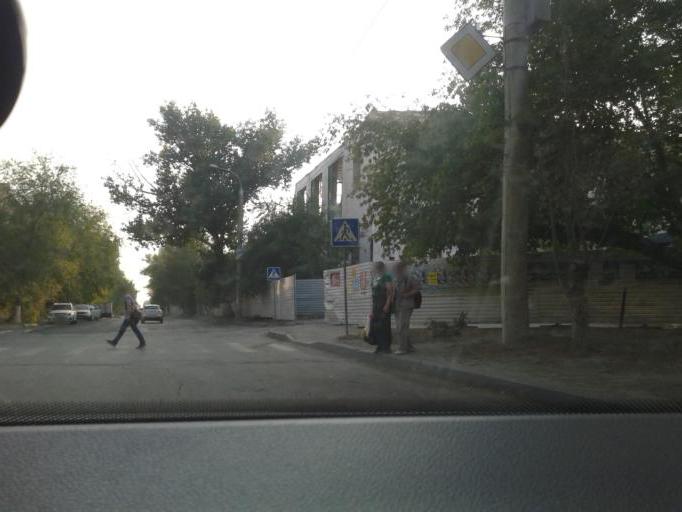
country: RU
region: Volgograd
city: Volgograd
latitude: 48.7003
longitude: 44.4993
